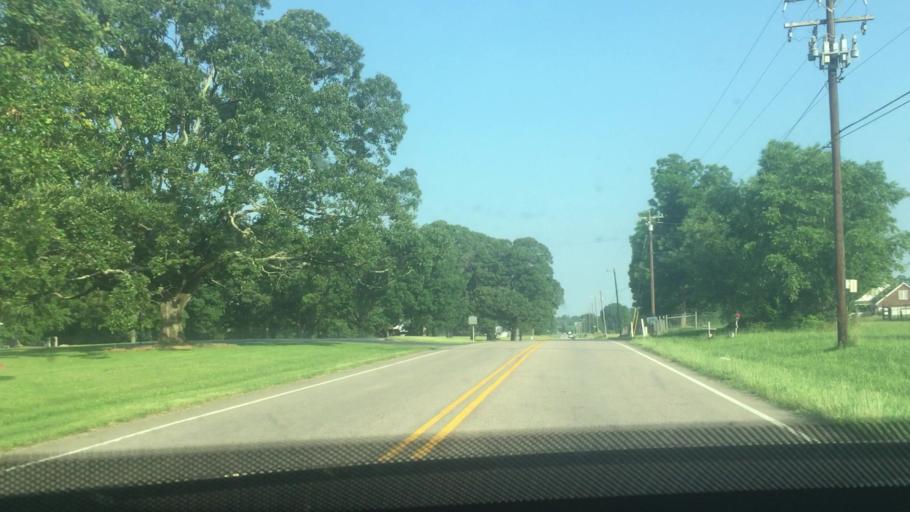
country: US
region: North Carolina
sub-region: Iredell County
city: Mooresville
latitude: 35.5854
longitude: -80.7432
